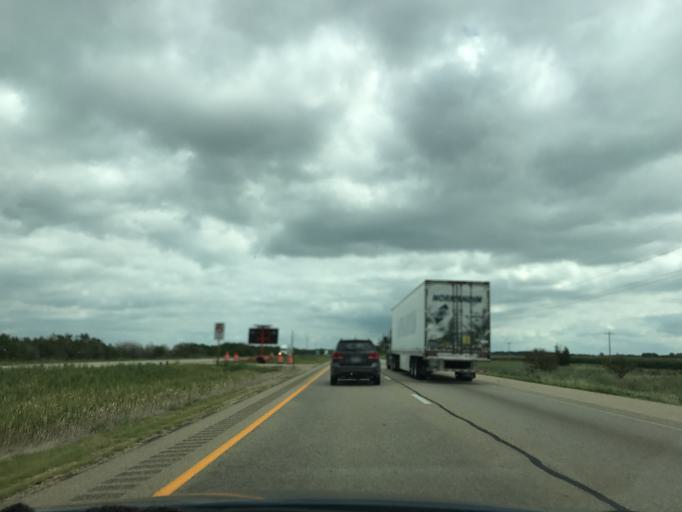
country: US
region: Illinois
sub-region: LaSalle County
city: Ottawa
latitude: 41.3683
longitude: -88.9036
